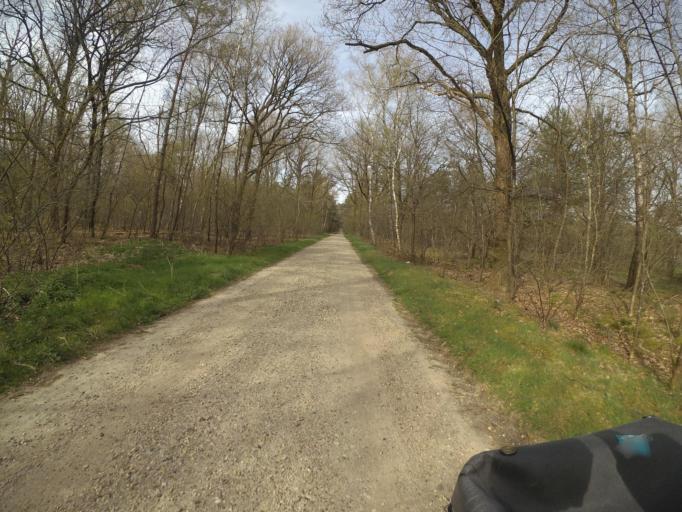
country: NL
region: Gelderland
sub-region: Gemeente Barneveld
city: Garderen
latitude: 52.2220
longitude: 5.7485
